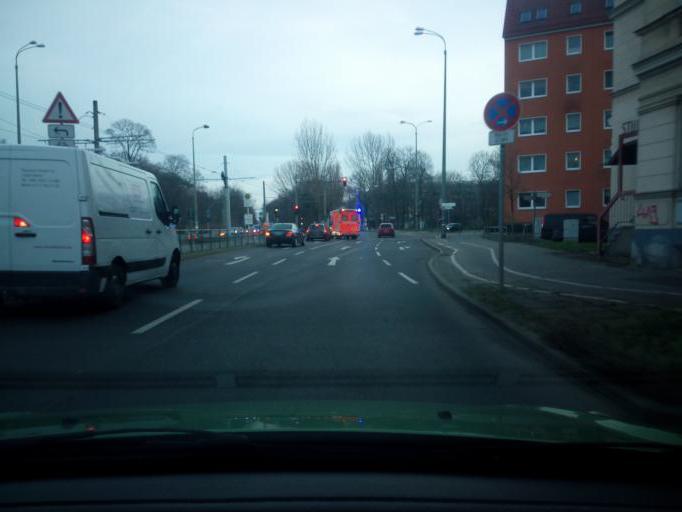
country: DE
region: Berlin
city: Berlin Koepenick
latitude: 52.4412
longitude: 13.5857
